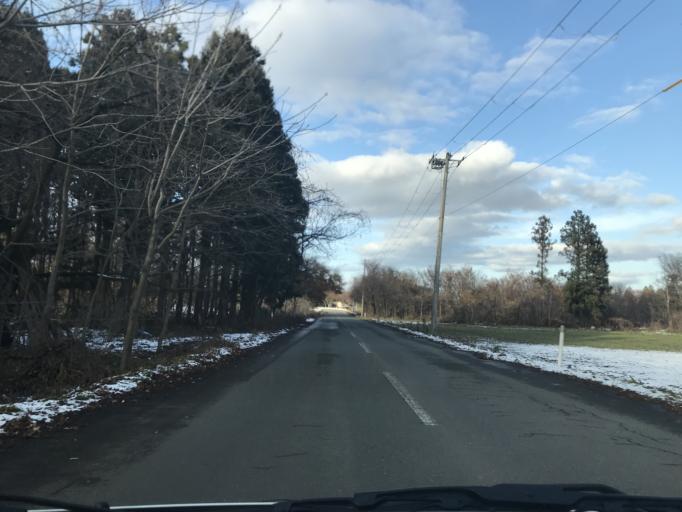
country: JP
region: Iwate
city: Kitakami
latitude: 39.2530
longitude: 141.0324
